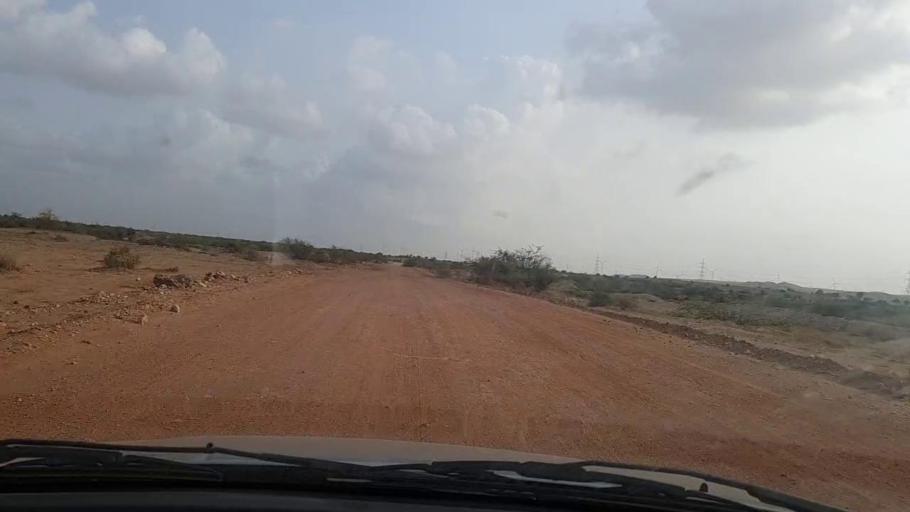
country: PK
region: Sindh
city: Thatta
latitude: 25.0767
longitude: 67.8933
